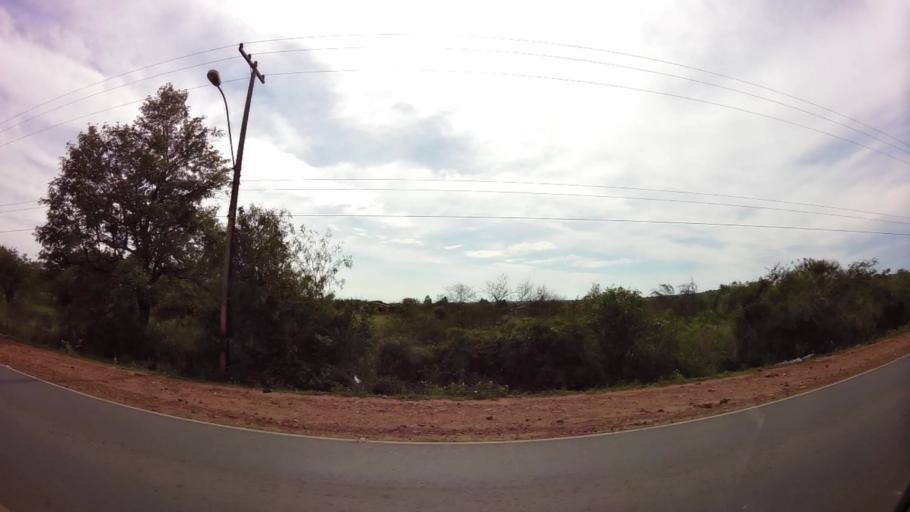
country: PY
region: Presidente Hayes
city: Villa Hayes
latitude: -25.1199
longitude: -57.4870
